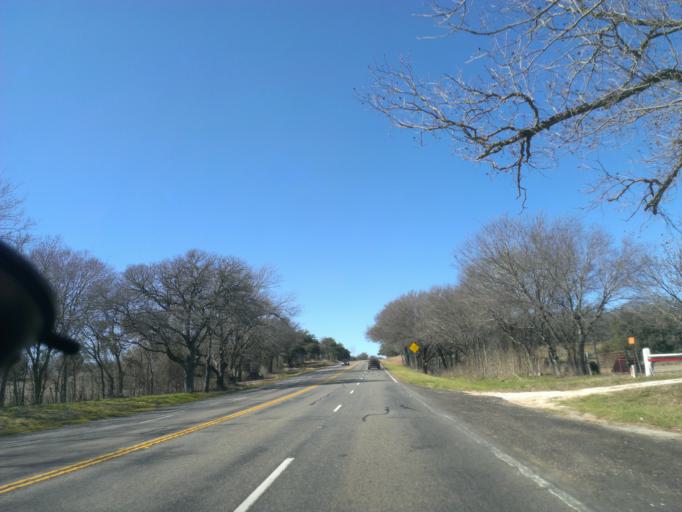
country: US
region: Texas
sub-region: Lampasas County
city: Kempner
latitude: 30.9275
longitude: -97.9954
